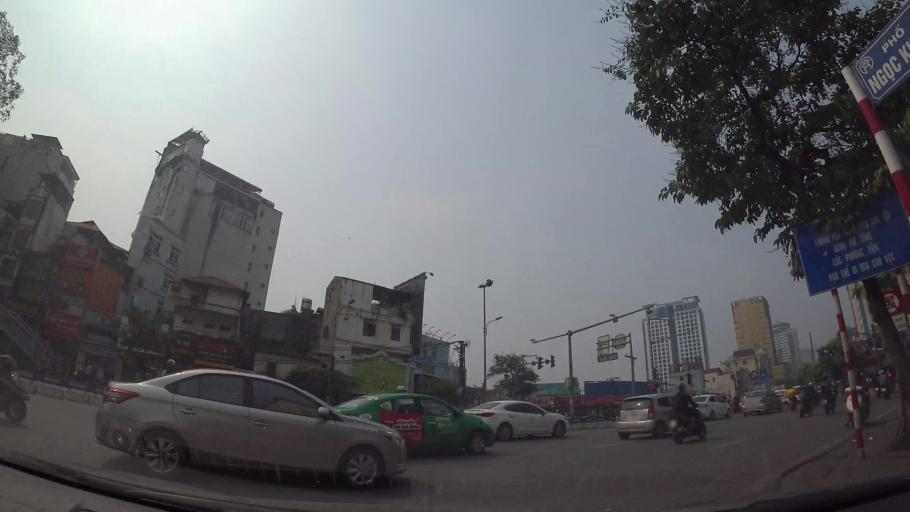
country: VN
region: Ha Noi
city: Dong Da
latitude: 21.0239
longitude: 105.8199
